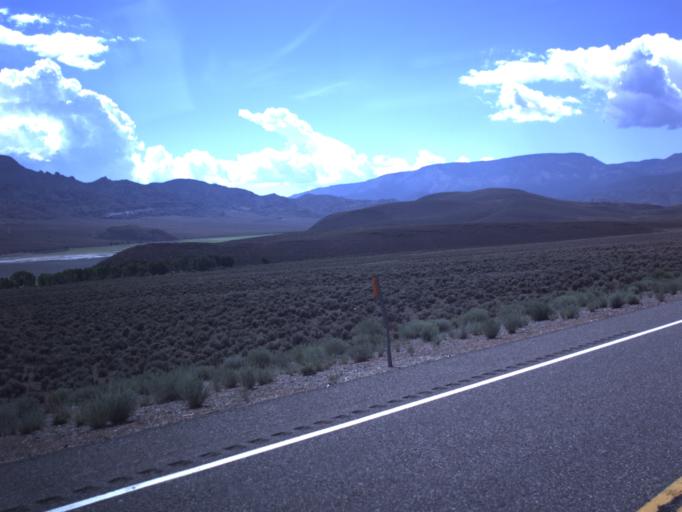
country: US
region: Utah
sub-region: Piute County
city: Junction
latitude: 38.2905
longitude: -112.2254
